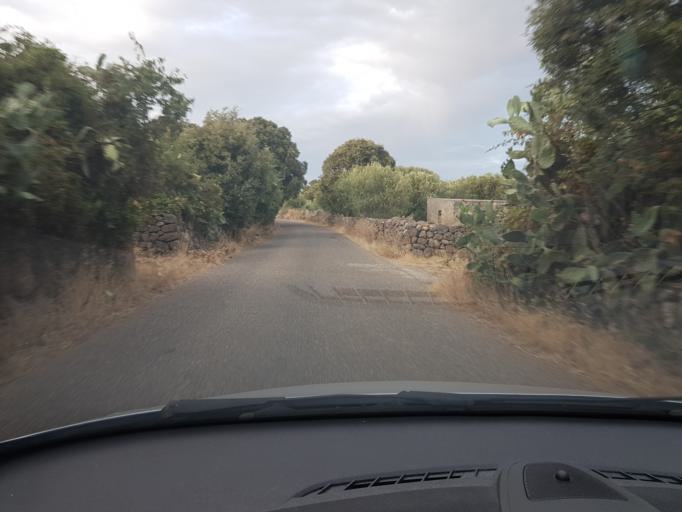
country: IT
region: Sardinia
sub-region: Provincia di Oristano
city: Seneghe
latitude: 40.0866
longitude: 8.6189
